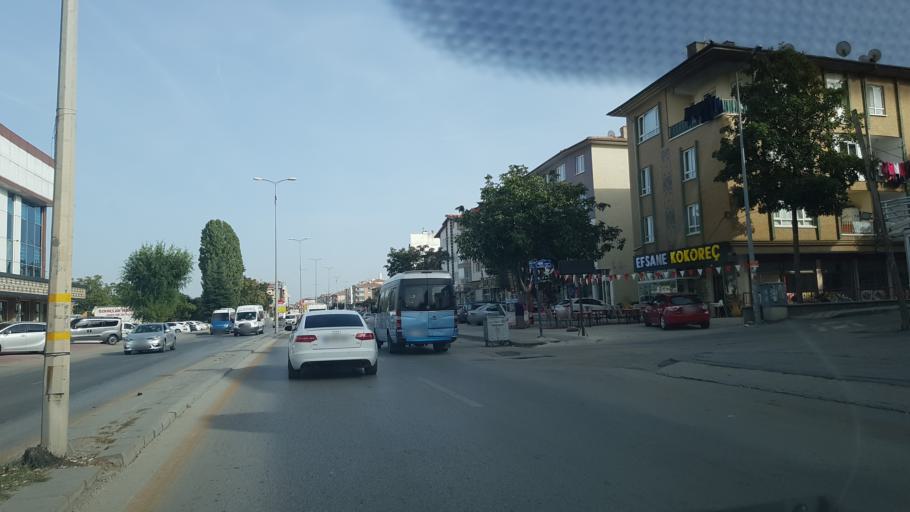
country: TR
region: Ankara
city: Etimesgut
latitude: 39.9517
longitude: 32.6469
